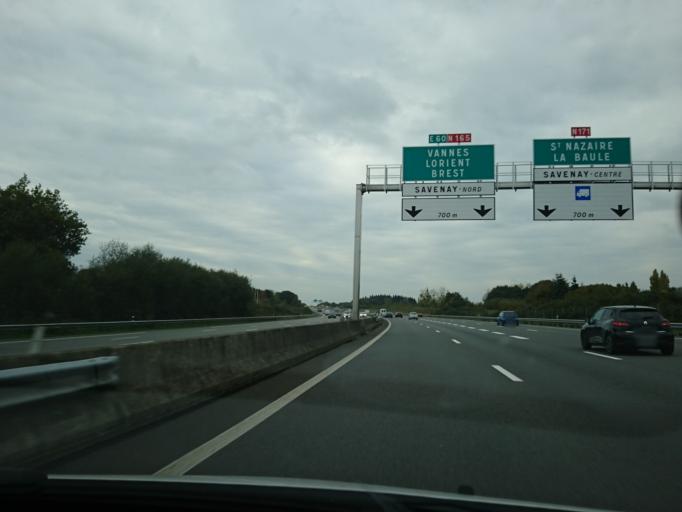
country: FR
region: Pays de la Loire
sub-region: Departement de la Loire-Atlantique
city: Savenay
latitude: 47.3681
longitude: -1.9108
